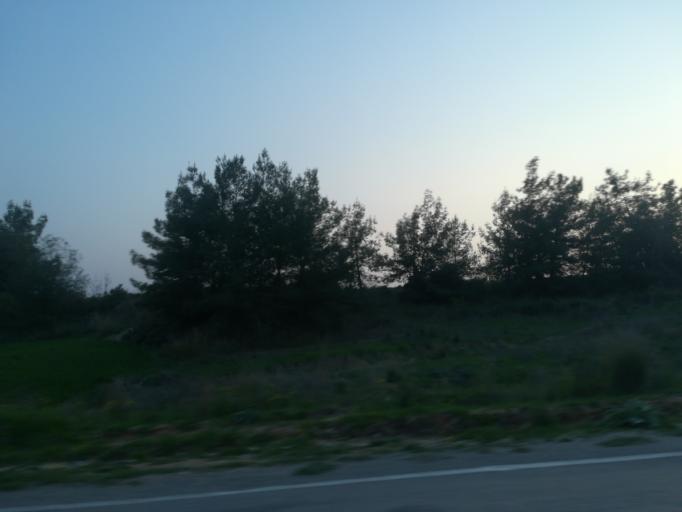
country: TR
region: Adana
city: Adana
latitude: 37.0747
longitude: 35.4036
